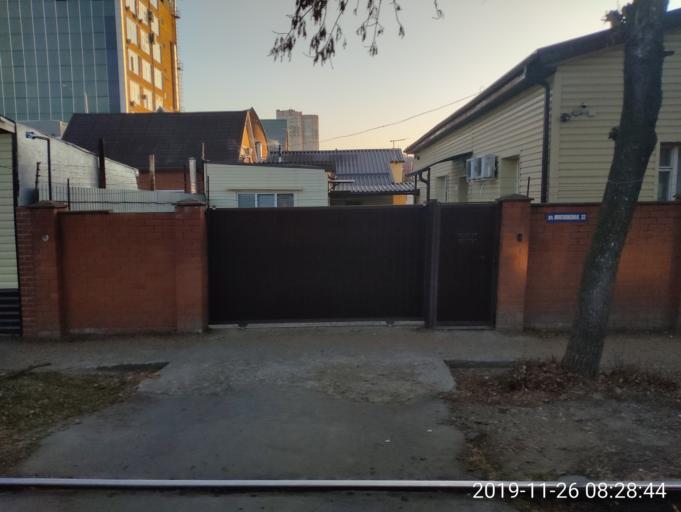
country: RU
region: Krasnodarskiy
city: Krasnodar
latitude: 45.0542
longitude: 39.0027
